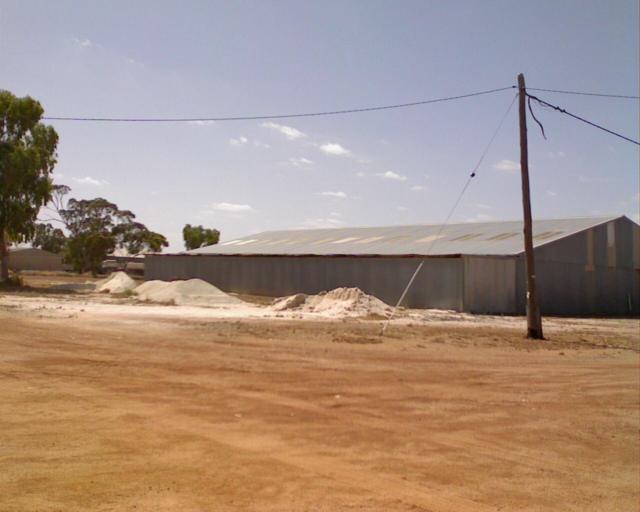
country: AU
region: Western Australia
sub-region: Merredin
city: Merredin
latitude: -30.9123
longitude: 118.2066
